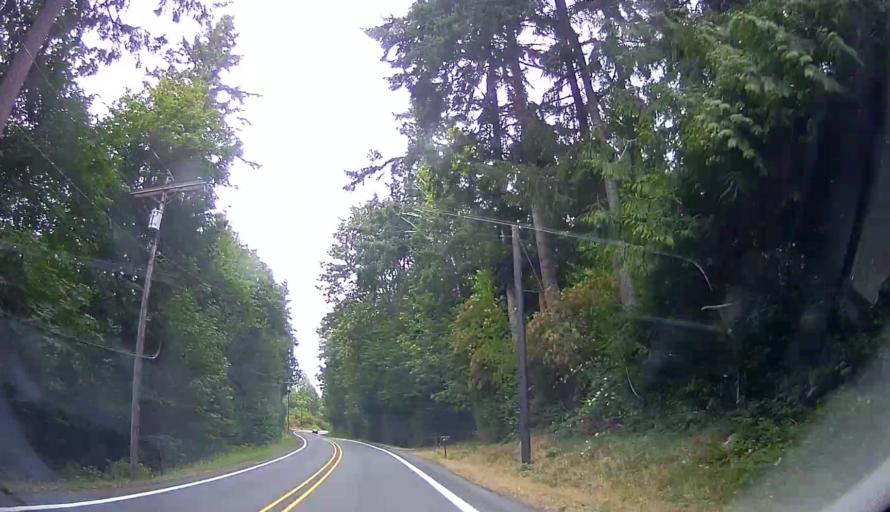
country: US
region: Washington
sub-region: Snohomish County
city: Warm Beach
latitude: 48.1438
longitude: -122.3580
